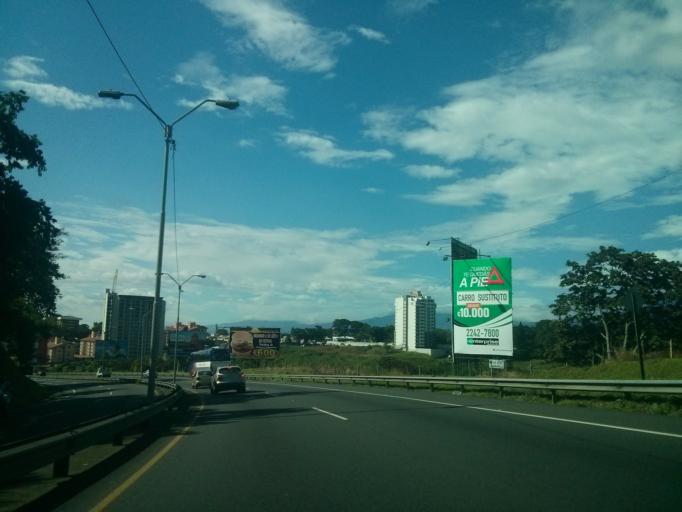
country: CR
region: San Jose
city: Colima
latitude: 9.9422
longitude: -84.0990
